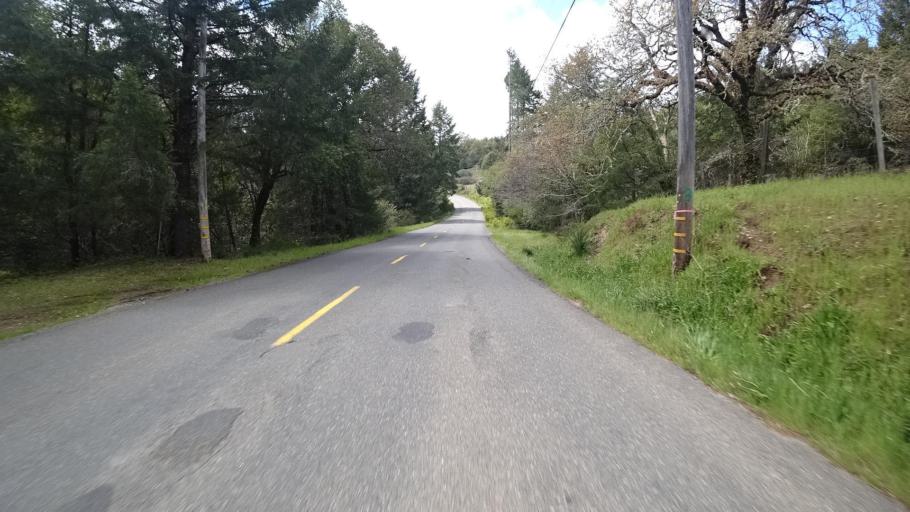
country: US
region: California
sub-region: Humboldt County
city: Redway
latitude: 40.0680
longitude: -123.9606
